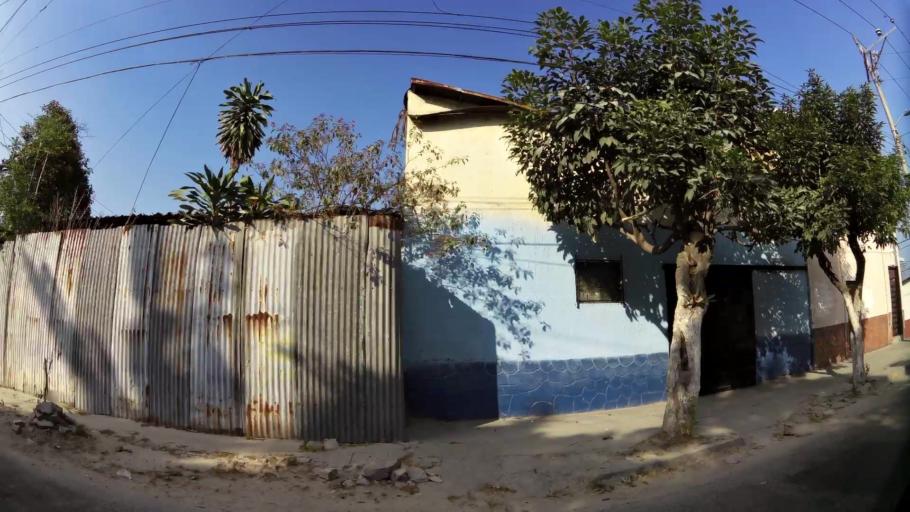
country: SV
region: San Salvador
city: San Salvador
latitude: 13.6972
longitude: -89.1781
